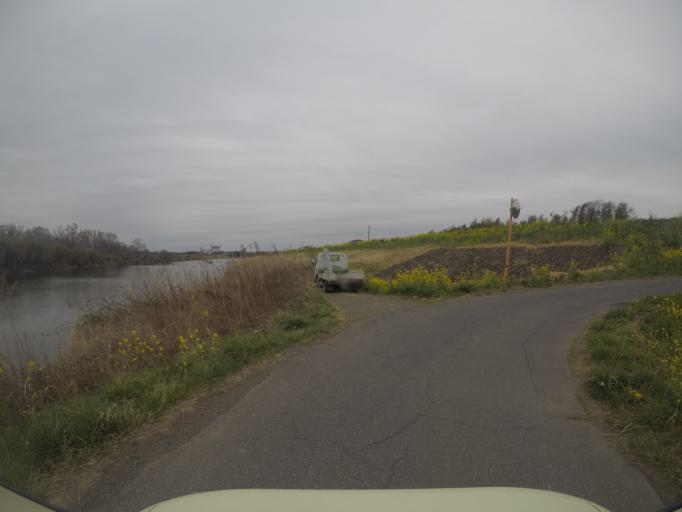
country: JP
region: Ibaraki
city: Ishige
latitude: 36.0847
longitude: 139.9997
